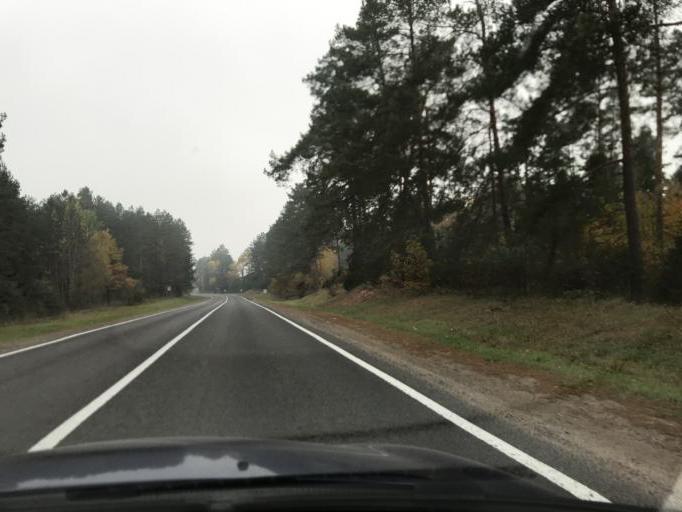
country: BY
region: Grodnenskaya
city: Hrodna
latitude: 53.8335
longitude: 23.8890
